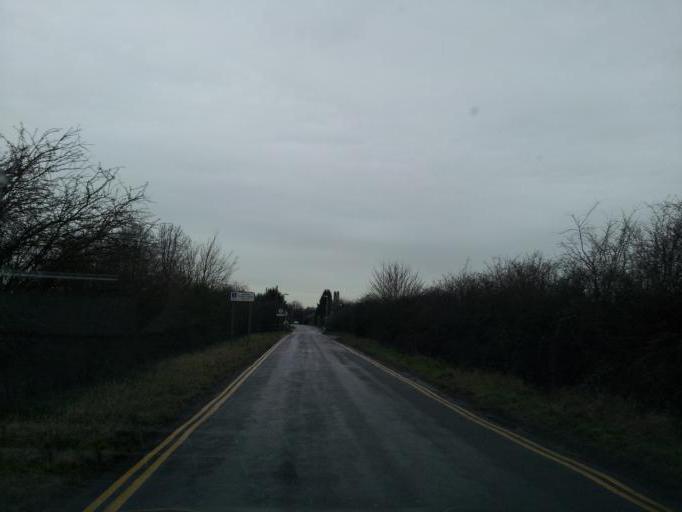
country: GB
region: England
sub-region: Cambridgeshire
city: Cambridge
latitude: 52.1734
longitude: 0.1551
